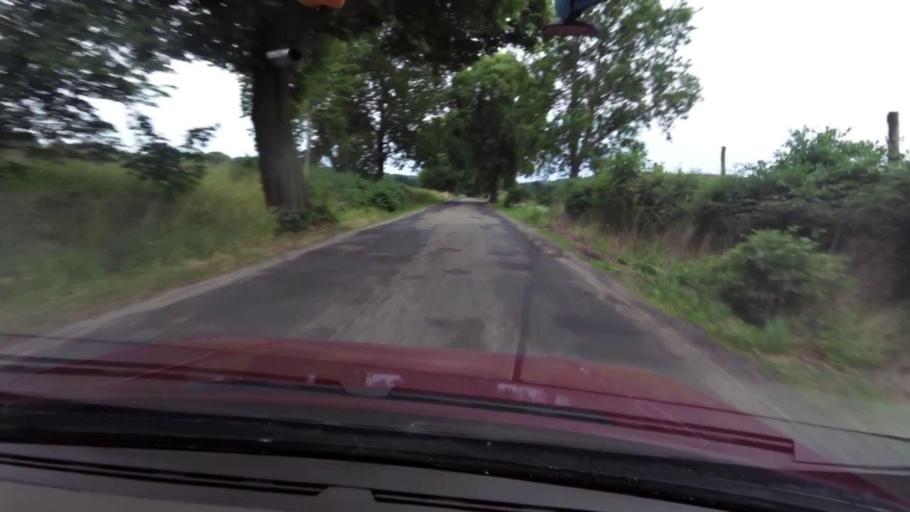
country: PL
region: Pomeranian Voivodeship
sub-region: Powiat slupski
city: Kepice
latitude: 54.2180
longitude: 16.8391
